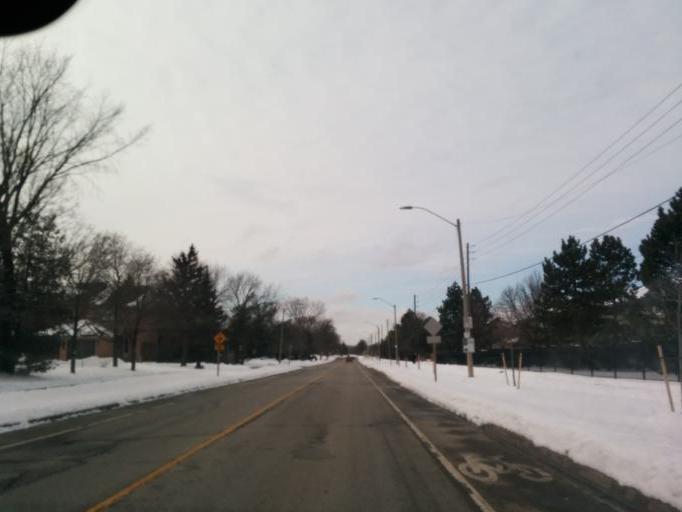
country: CA
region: Ontario
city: Mississauga
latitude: 43.5369
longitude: -79.6695
